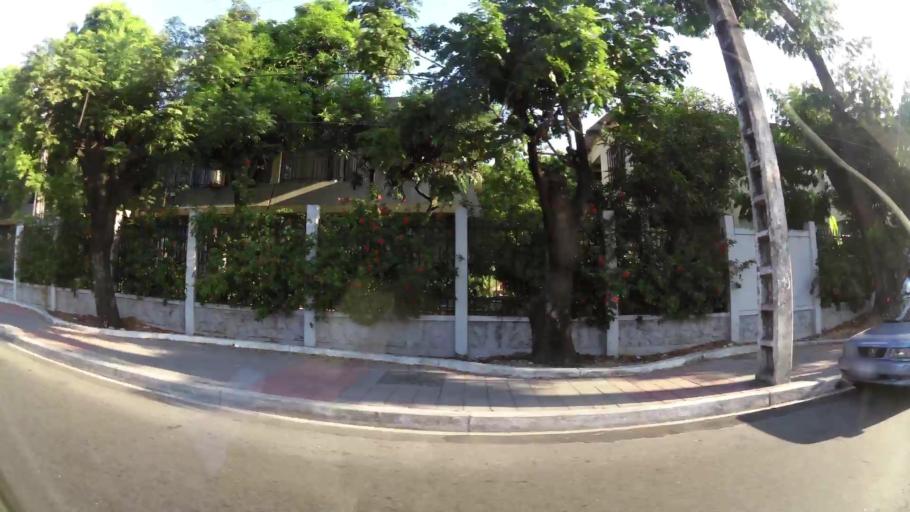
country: EC
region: Guayas
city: Guayaquil
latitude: -2.1784
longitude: -79.9011
